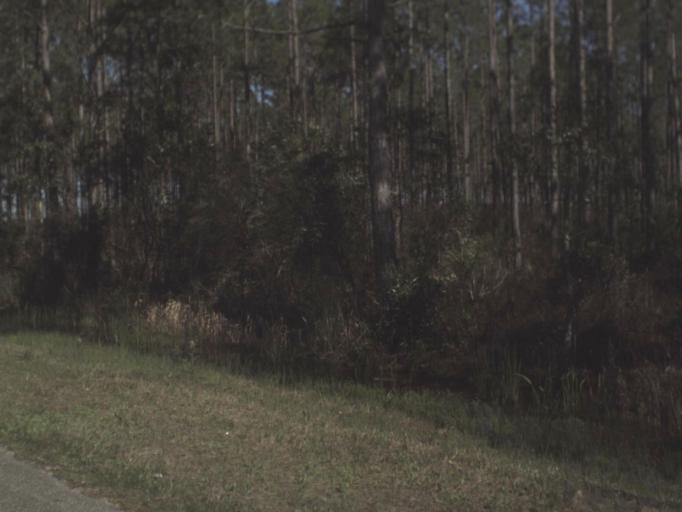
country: US
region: Florida
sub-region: Gulf County
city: Port Saint Joe
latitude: 29.8679
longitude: -85.2360
